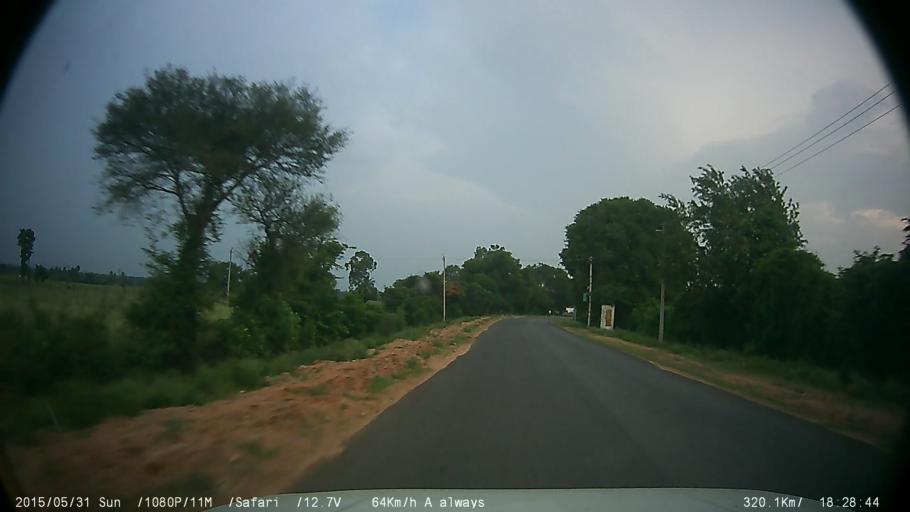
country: IN
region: Karnataka
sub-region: Mysore
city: Nanjangud
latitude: 12.1222
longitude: 76.7250
